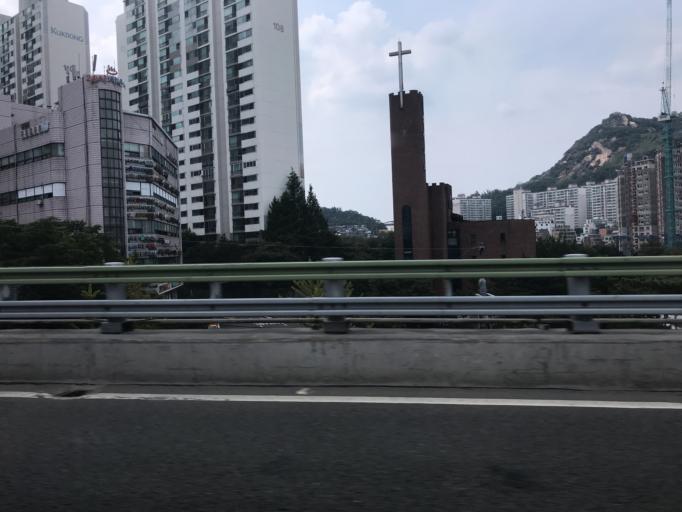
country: KR
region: Seoul
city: Seoul
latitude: 37.5717
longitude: 126.9594
